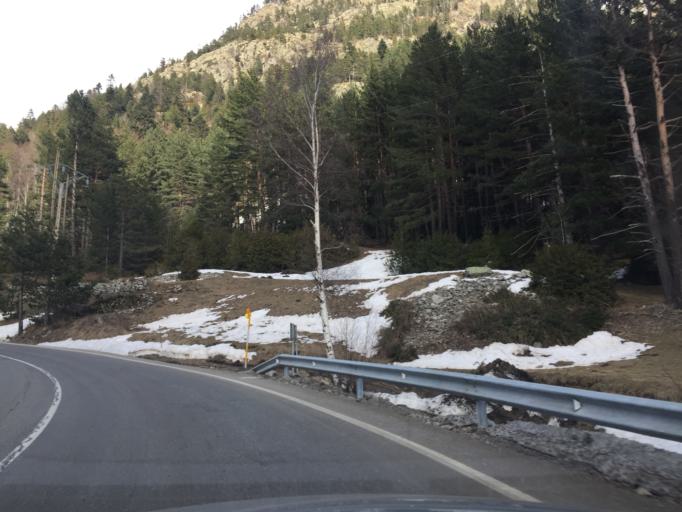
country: ES
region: Aragon
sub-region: Provincia de Huesca
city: Bielsa
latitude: 42.7032
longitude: 0.2018
